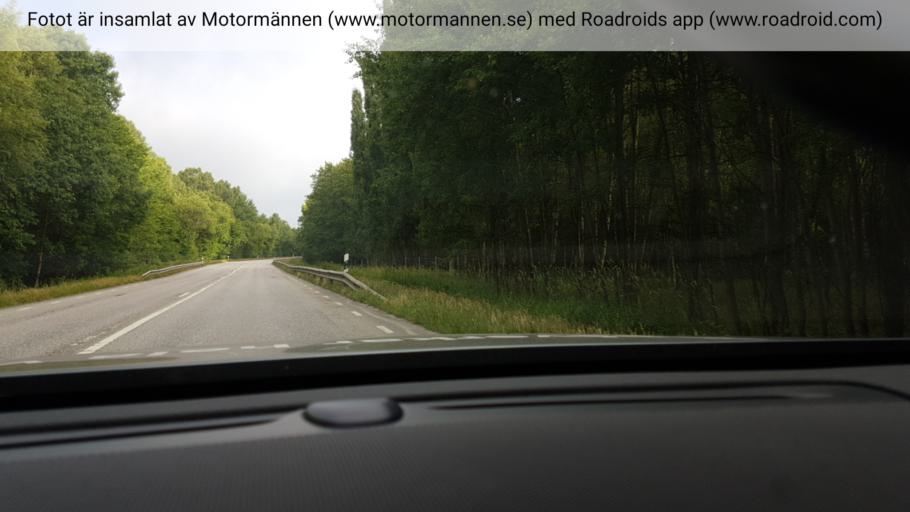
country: SE
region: Skane
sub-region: Hassleholms Kommun
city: Bjarnum
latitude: 56.2721
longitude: 13.7163
